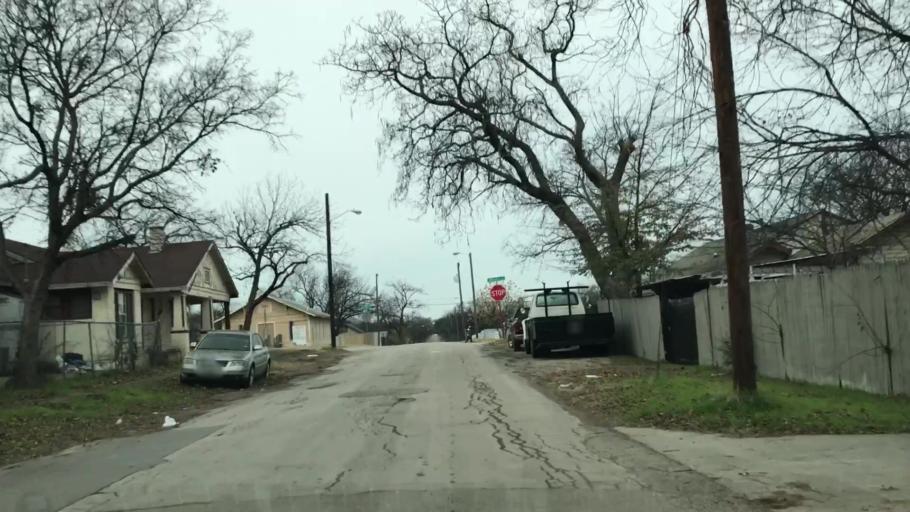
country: US
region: Texas
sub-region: Dallas County
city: Dallas
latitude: 32.7150
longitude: -96.8139
